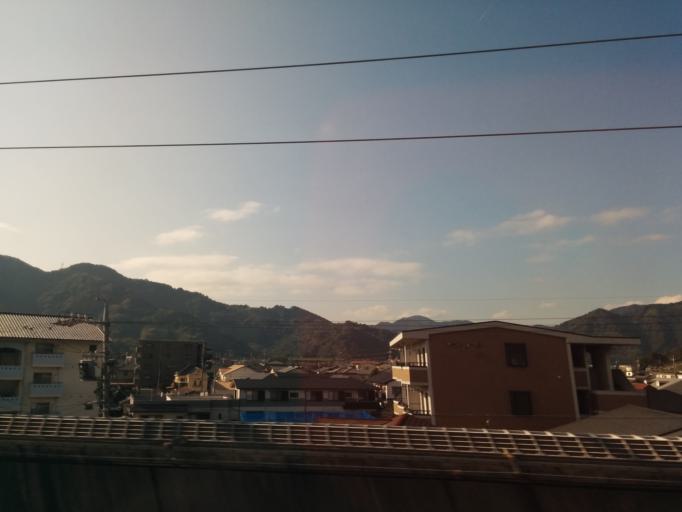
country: JP
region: Shizuoka
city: Shizuoka-shi
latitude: 34.9448
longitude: 138.3637
